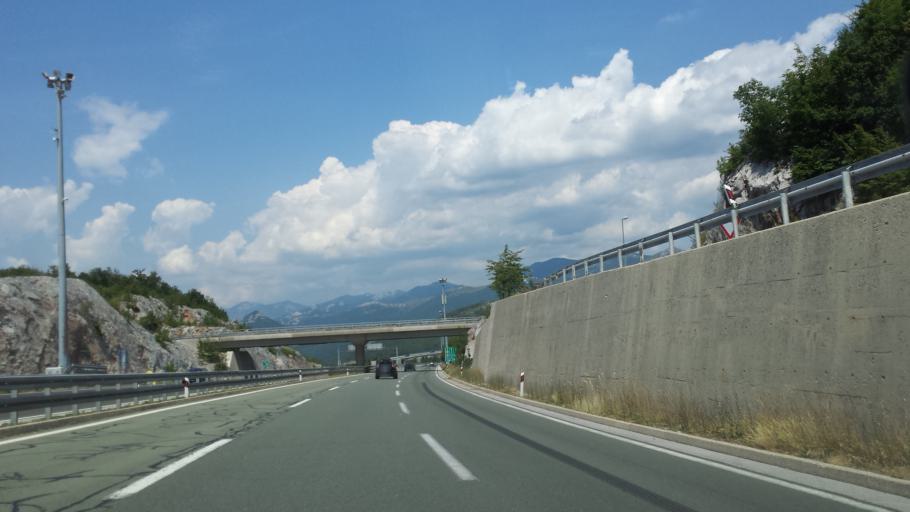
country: HR
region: Primorsko-Goranska
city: Krasica
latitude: 45.3334
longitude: 14.5974
